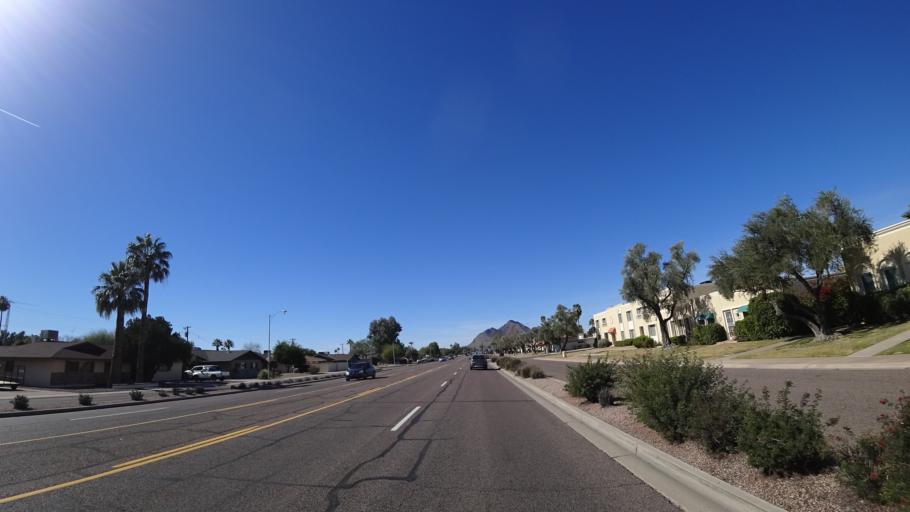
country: US
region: Arizona
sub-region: Maricopa County
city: Scottsdale
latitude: 33.5094
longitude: -111.9014
